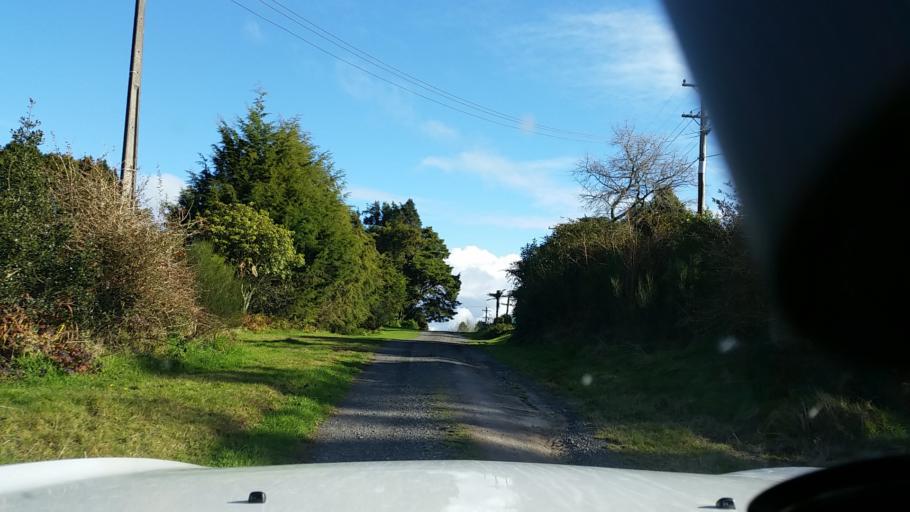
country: NZ
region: Bay of Plenty
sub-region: Rotorua District
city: Rotorua
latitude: -38.1006
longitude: 176.0811
